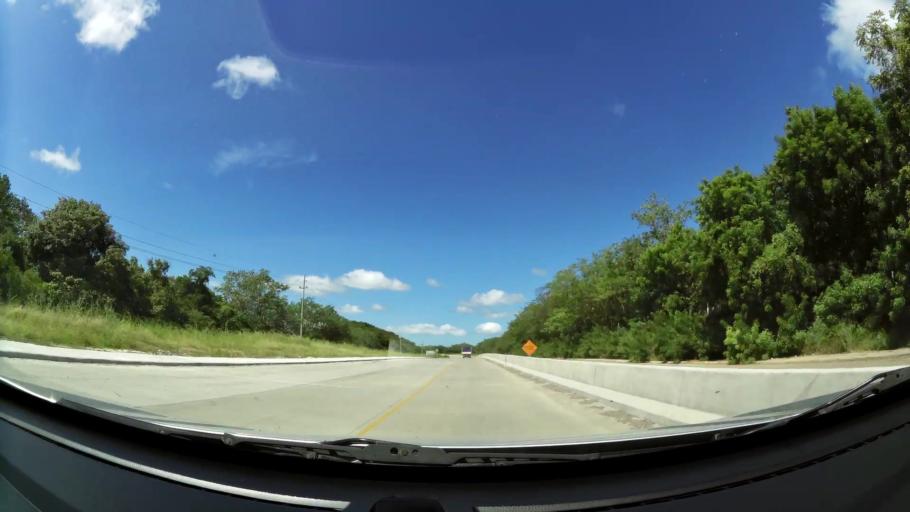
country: CR
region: Guanacaste
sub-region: Canton de Canas
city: Canas
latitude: 10.4433
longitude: -85.1115
